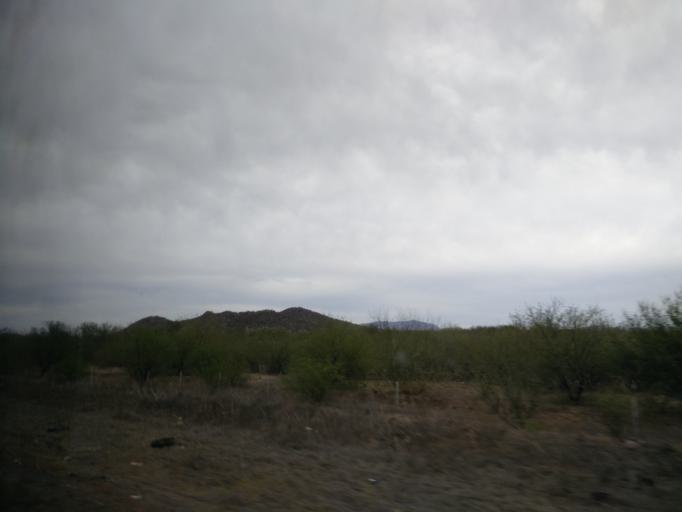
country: MX
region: Sonora
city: Hermosillo
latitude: 28.8395
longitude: -110.9582
